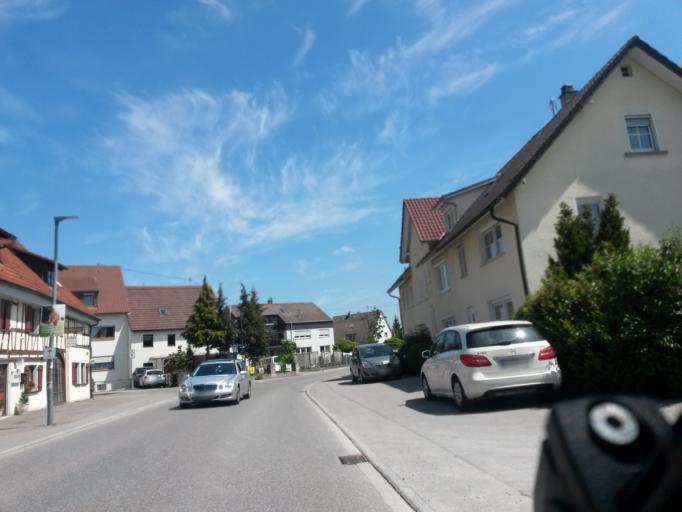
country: DE
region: Baden-Wuerttemberg
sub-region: Tuebingen Region
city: Bad Waldsee
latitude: 47.9215
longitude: 9.7376
